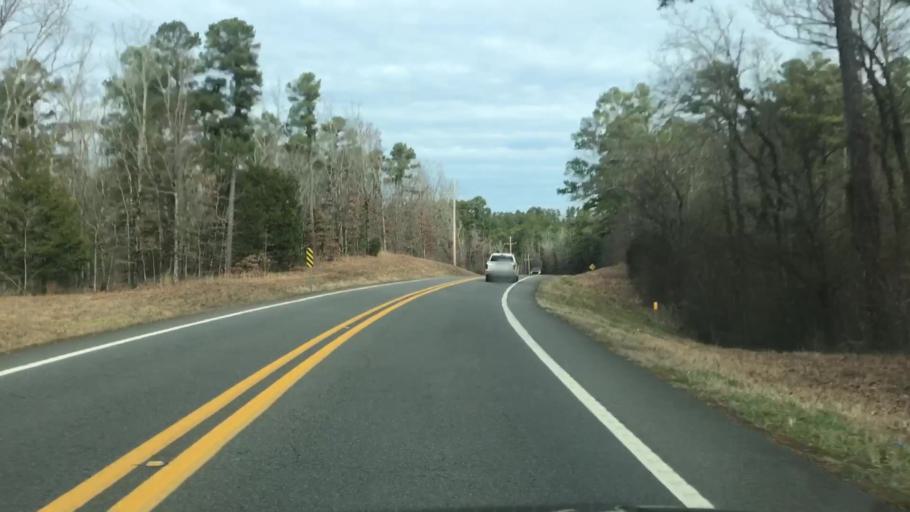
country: US
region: Arkansas
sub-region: Montgomery County
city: Mount Ida
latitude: 34.5890
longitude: -93.6640
